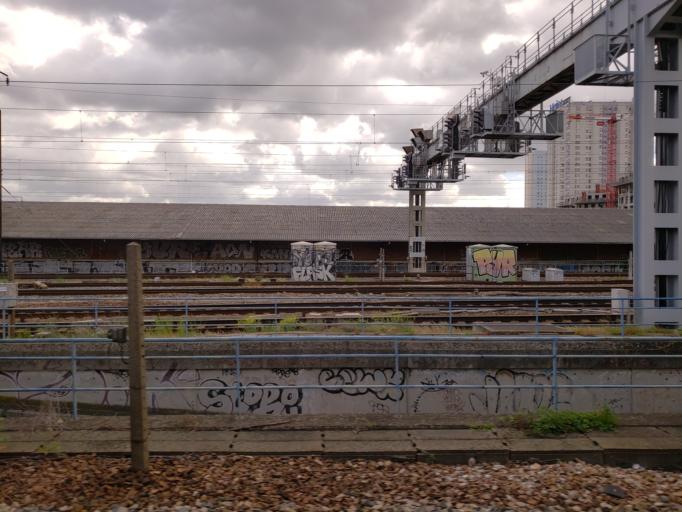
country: FR
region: Ile-de-France
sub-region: Paris
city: Saint-Ouen
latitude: 48.8990
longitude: 2.3547
